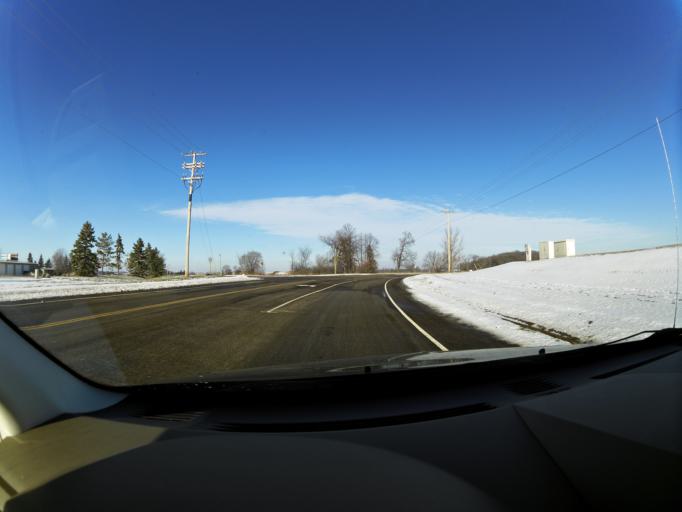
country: US
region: Minnesota
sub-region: Olmsted County
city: Oronoco
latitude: 44.0918
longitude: -92.5087
